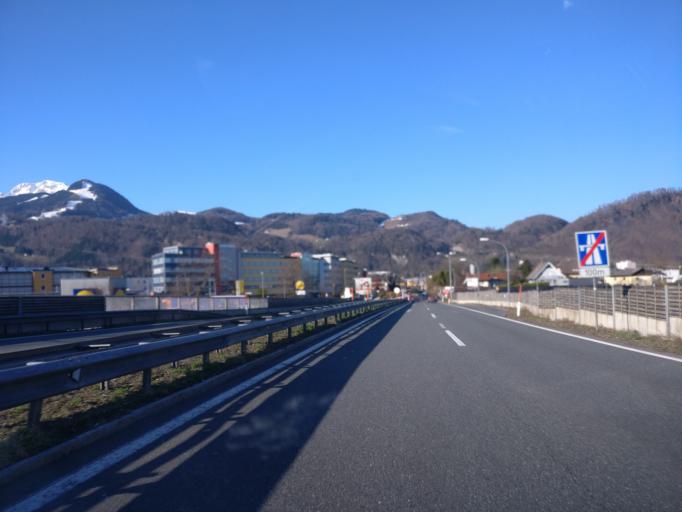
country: AT
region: Salzburg
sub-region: Politischer Bezirk Hallein
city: Hallein
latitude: 47.6878
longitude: 13.1099
